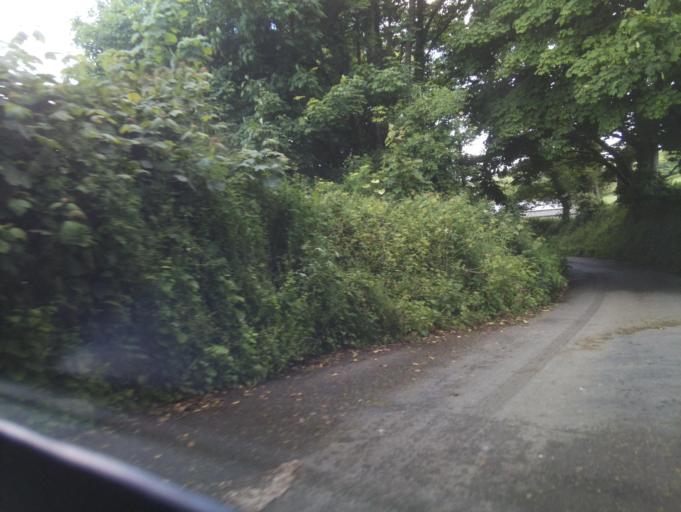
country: GB
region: England
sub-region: Devon
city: Dartmouth
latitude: 50.3566
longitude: -3.5496
